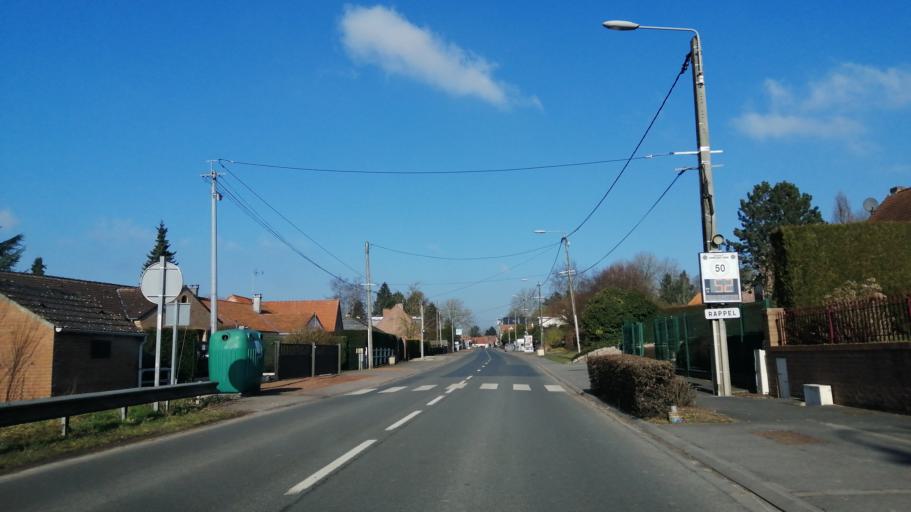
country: FR
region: Nord-Pas-de-Calais
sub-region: Departement du Pas-de-Calais
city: Mont-Saint-Eloi
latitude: 50.3694
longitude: 2.6416
